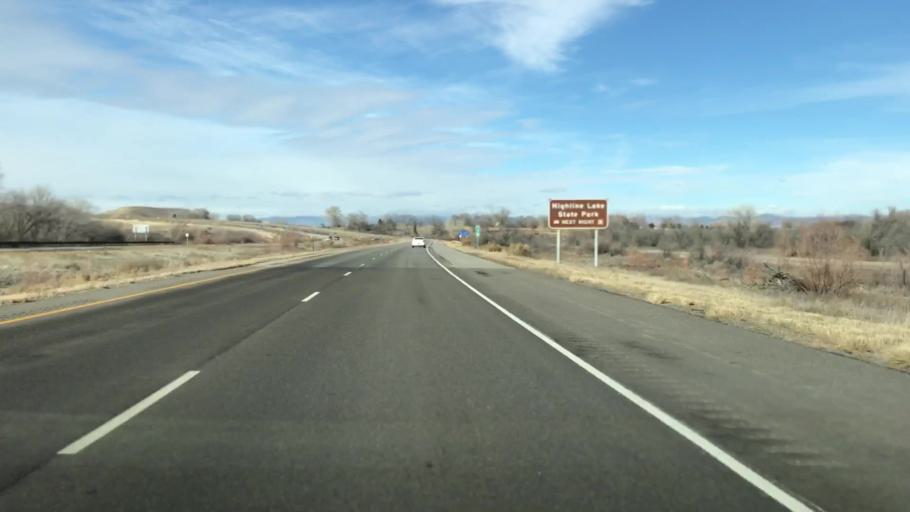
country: US
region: Colorado
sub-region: Mesa County
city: Loma
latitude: 39.1723
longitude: -108.7964
